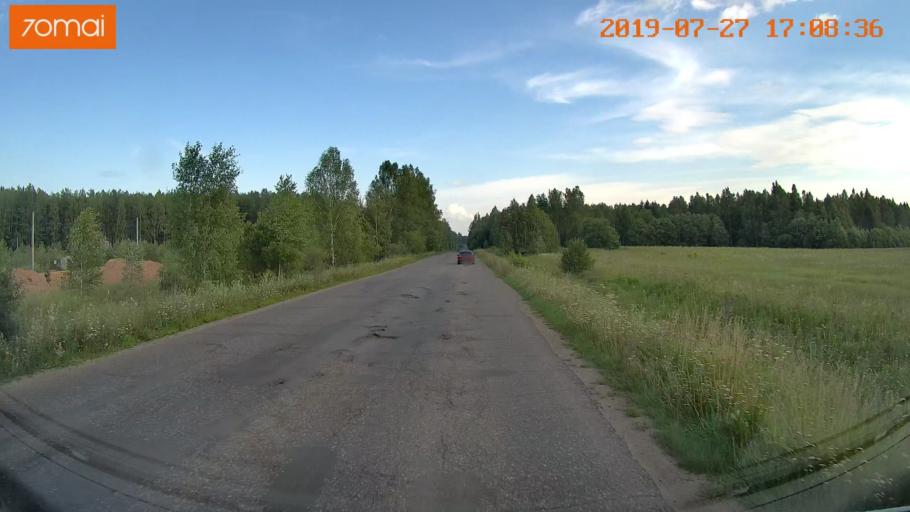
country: RU
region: Ivanovo
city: Novo-Talitsy
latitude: 57.0813
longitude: 40.8393
